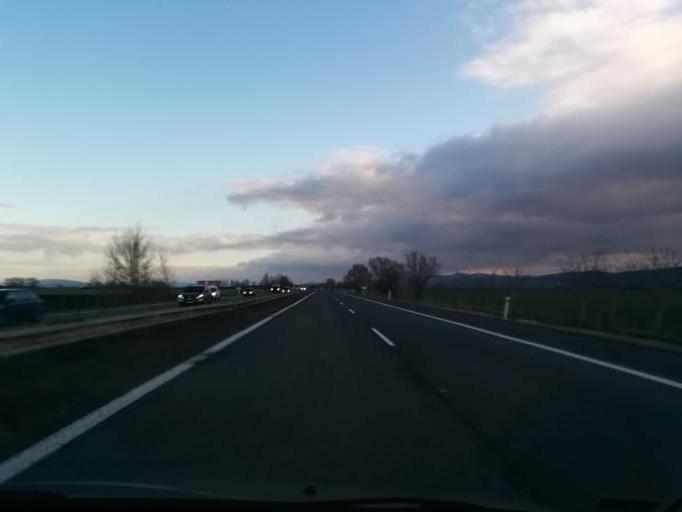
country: SK
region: Trnavsky
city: Leopoldov
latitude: 48.5114
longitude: 17.7712
